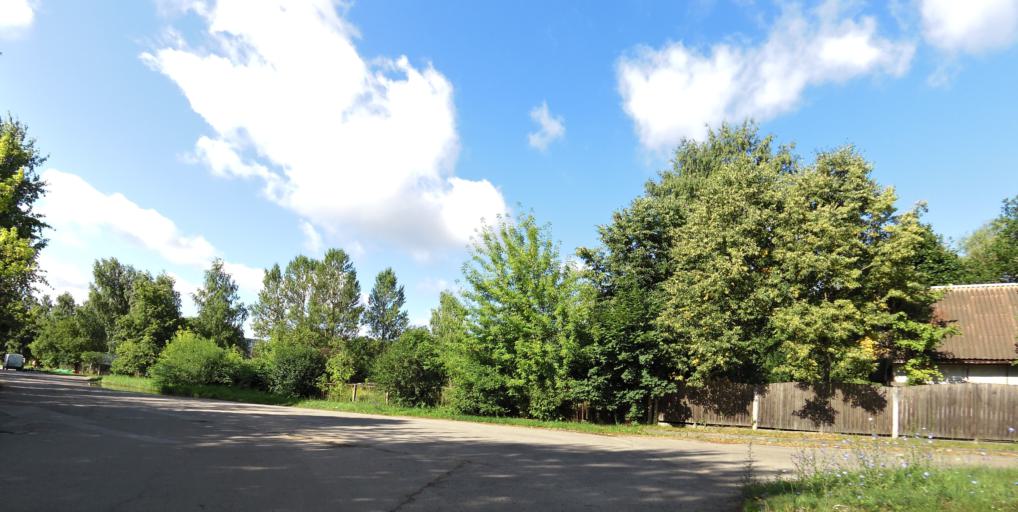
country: LT
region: Vilnius County
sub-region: Vilnius
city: Vilnius
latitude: 54.7092
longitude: 25.2724
